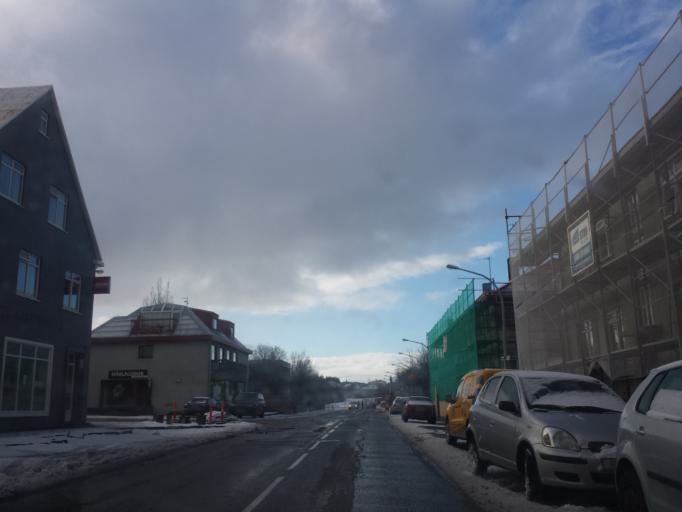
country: IS
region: Capital Region
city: Reykjavik
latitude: 64.1401
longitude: -21.9153
